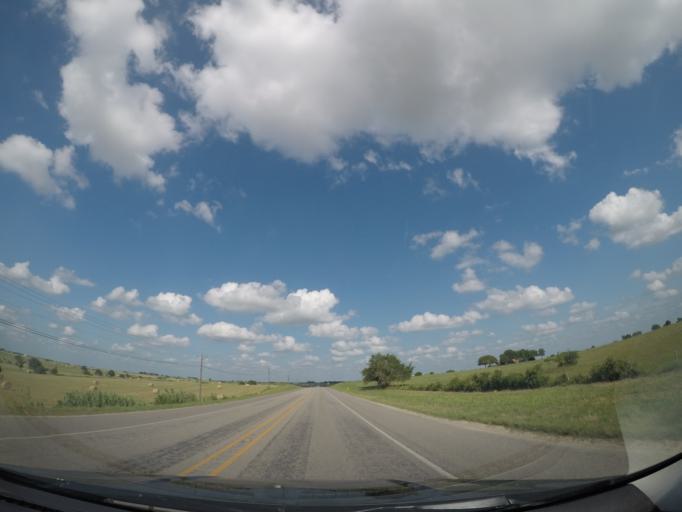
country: US
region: Texas
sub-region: Lavaca County
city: Shiner
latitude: 29.4535
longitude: -97.2284
